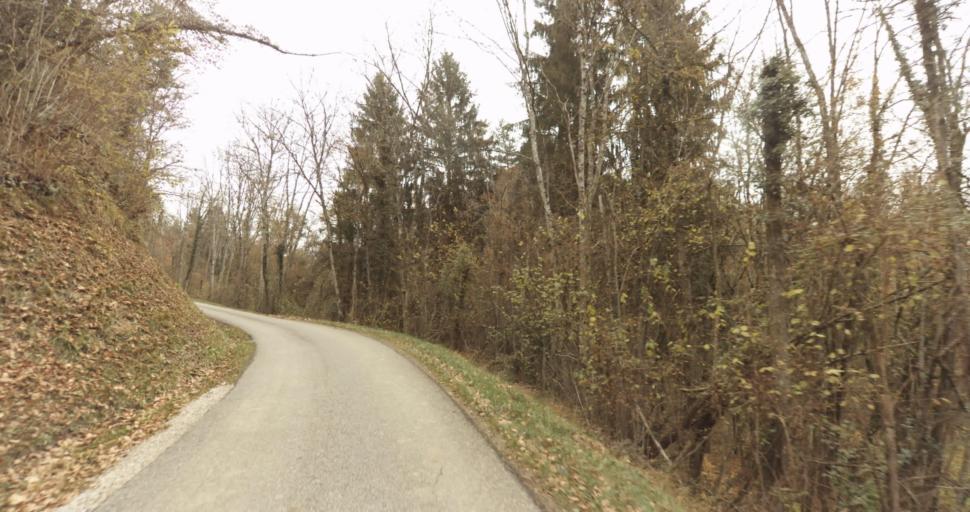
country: FR
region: Rhone-Alpes
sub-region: Departement de la Haute-Savoie
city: Chavanod
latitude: 45.9042
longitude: 6.0531
